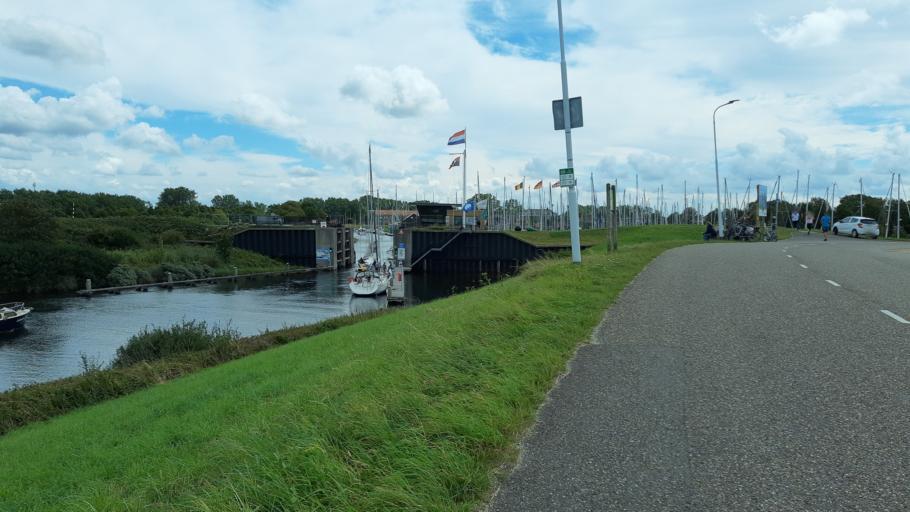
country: NL
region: Zeeland
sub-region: Schouwen-Duiveland
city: Scharendijke
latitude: 51.7305
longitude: 3.9124
